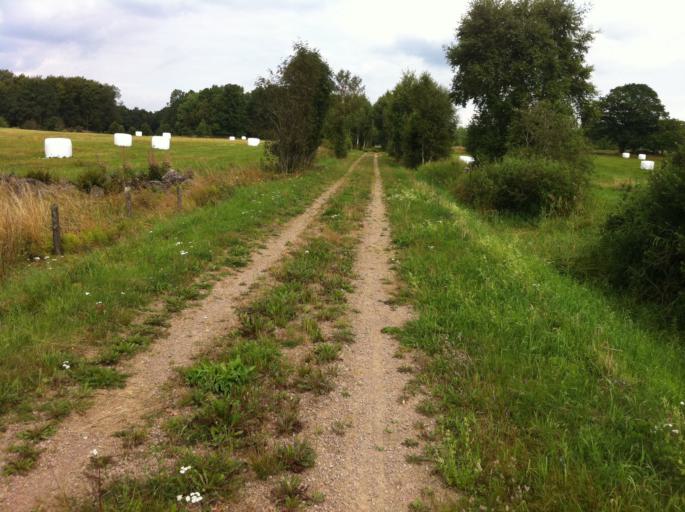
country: SE
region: Skane
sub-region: Horby Kommun
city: Hoerby
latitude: 55.9138
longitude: 13.7949
